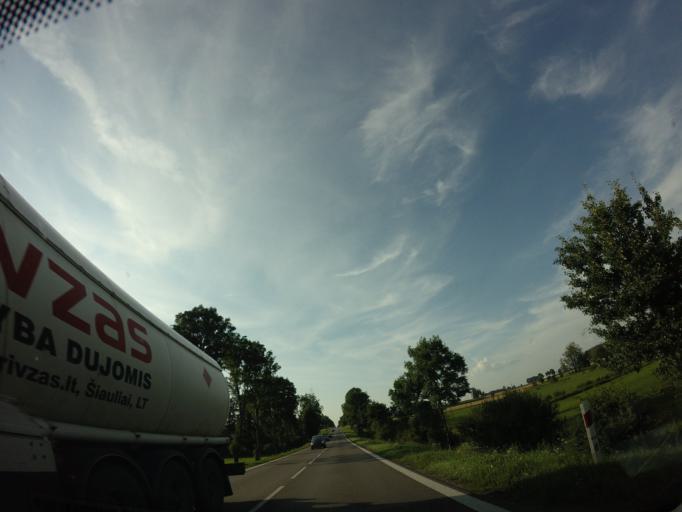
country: PL
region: Podlasie
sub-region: Powiat sokolski
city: Janow
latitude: 53.4152
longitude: 23.1160
